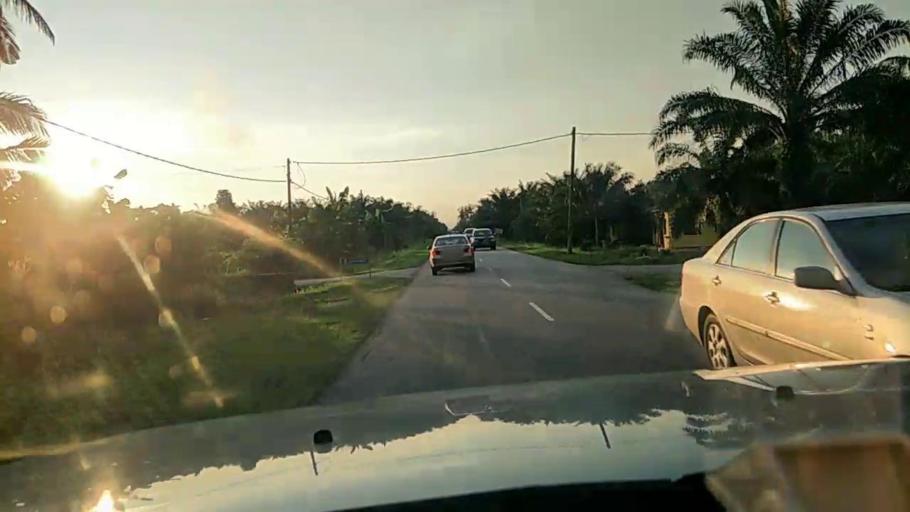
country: MY
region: Selangor
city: Kuala Selangor
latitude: 3.3121
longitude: 101.2867
